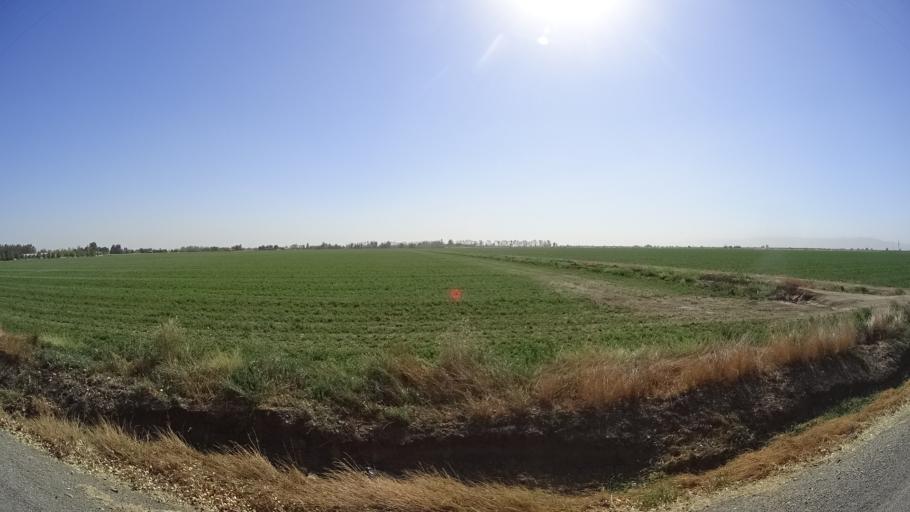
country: US
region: California
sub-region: Yolo County
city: Winters
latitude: 38.5906
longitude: -121.8723
